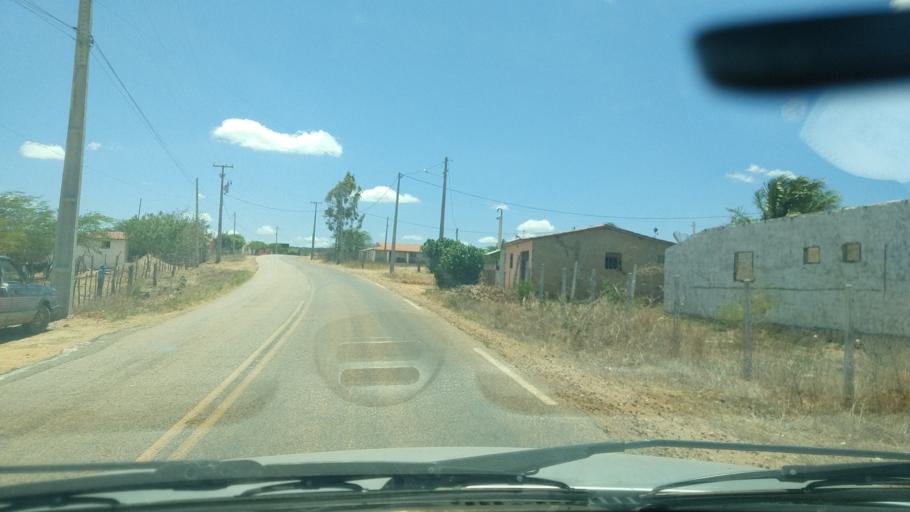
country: BR
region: Rio Grande do Norte
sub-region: Cerro Cora
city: Cerro Cora
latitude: -6.0582
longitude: -36.3616
